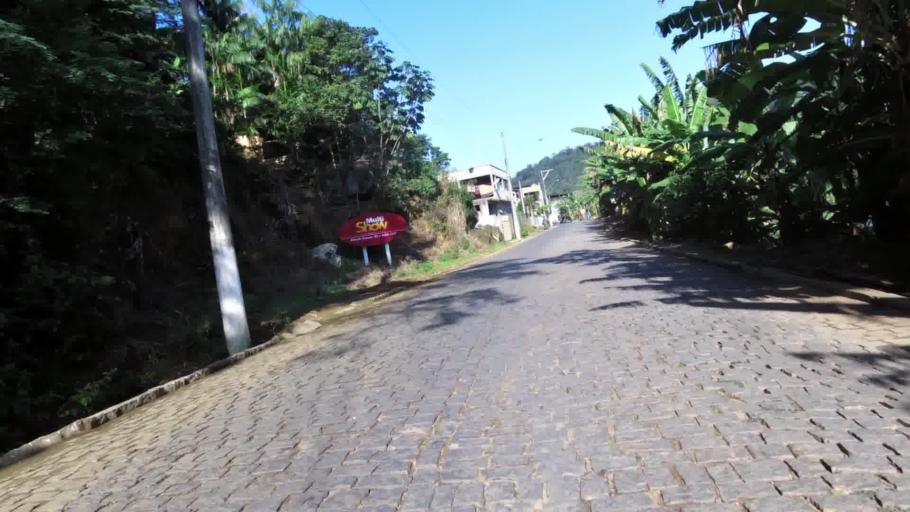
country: BR
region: Espirito Santo
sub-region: Alfredo Chaves
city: Alfredo Chaves
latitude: -20.6275
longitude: -40.7668
